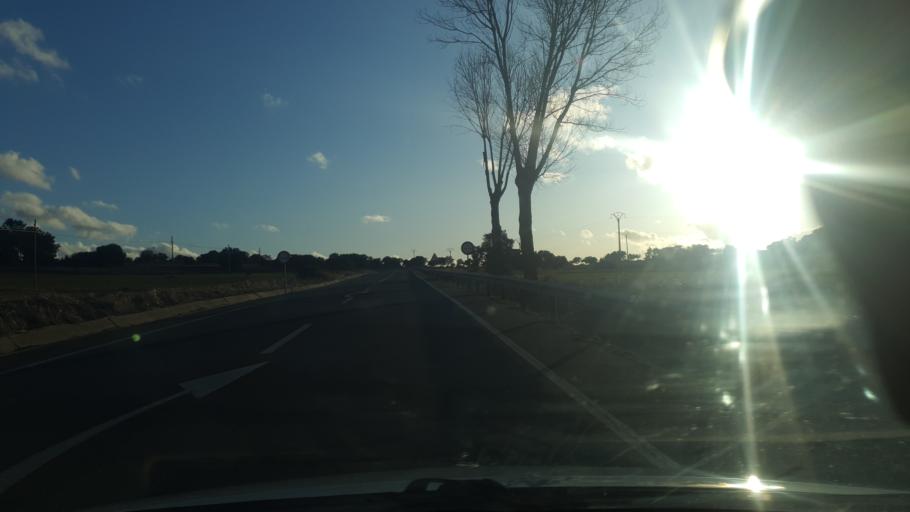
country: ES
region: Castille and Leon
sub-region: Provincia de Avila
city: Mingorria
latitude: 40.7403
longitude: -4.6731
